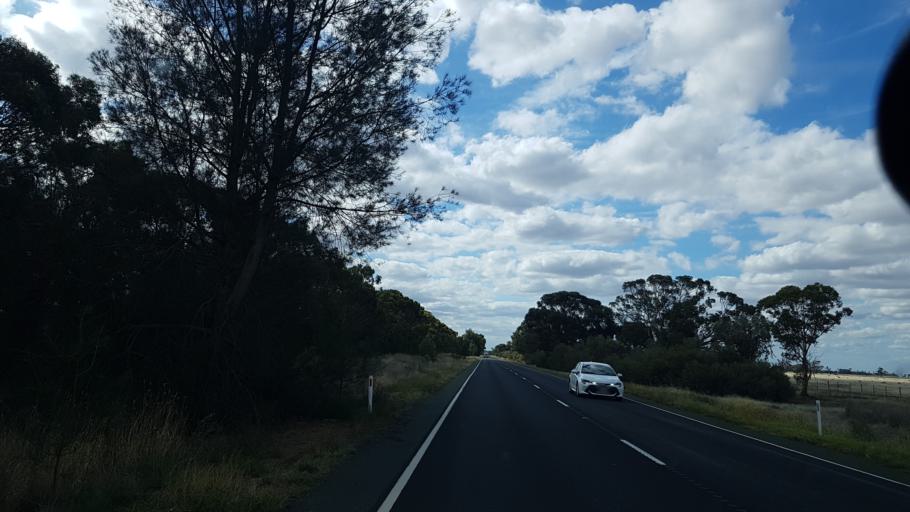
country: AU
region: Victoria
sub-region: Swan Hill
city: Swan Hill
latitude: -35.9816
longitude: 143.9451
